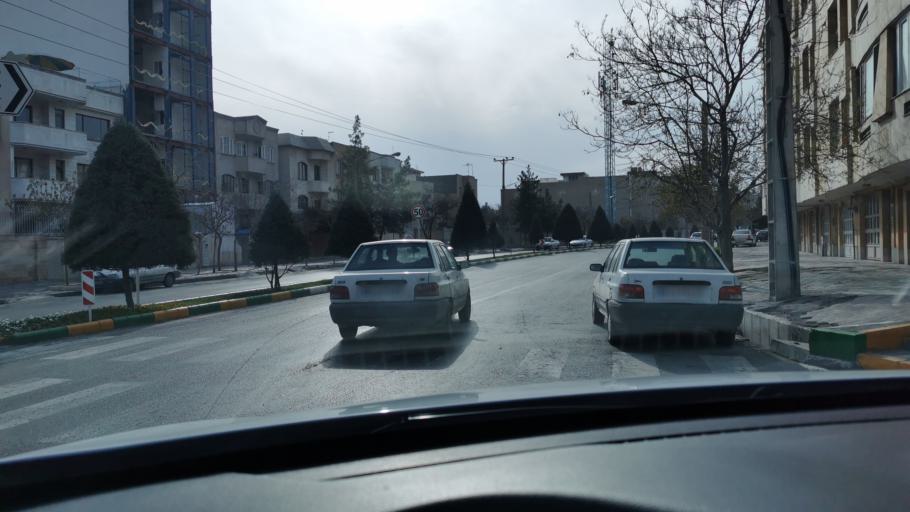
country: IR
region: Razavi Khorasan
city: Mashhad
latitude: 36.3125
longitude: 59.5152
